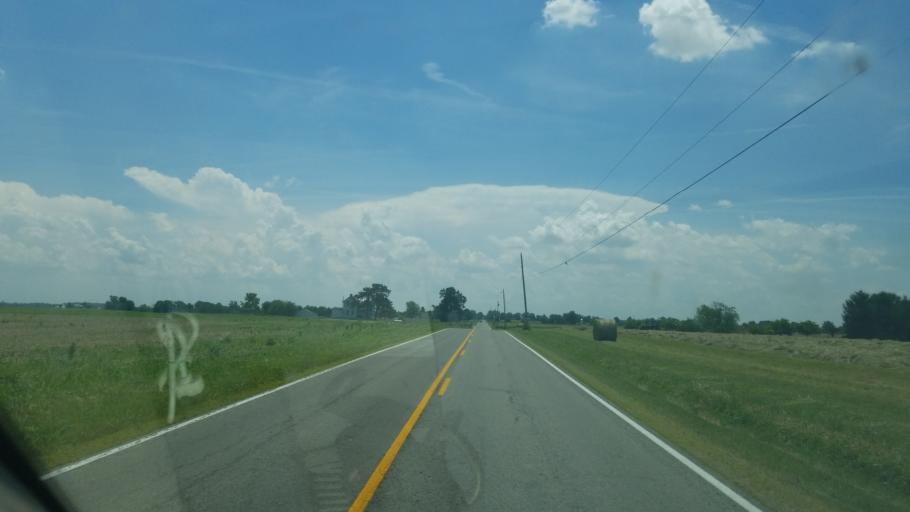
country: US
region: Ohio
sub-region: Hancock County
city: Arlington
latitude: 40.9496
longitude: -83.5942
